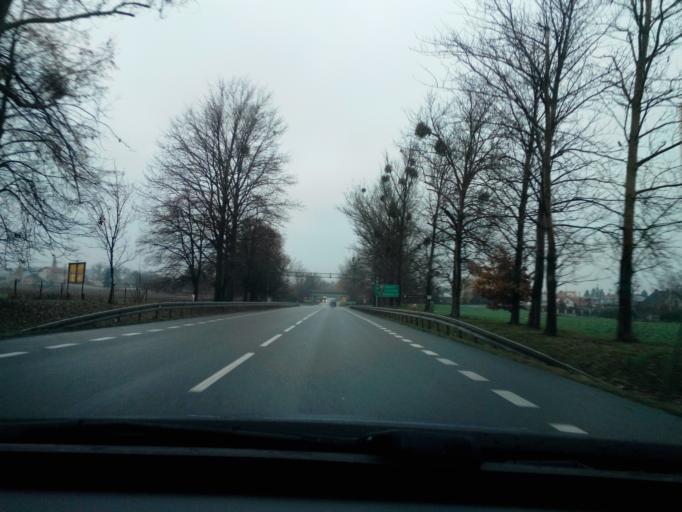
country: PL
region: Pomeranian Voivodeship
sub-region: Powiat tczewski
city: Subkowy
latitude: 54.0454
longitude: 18.7608
